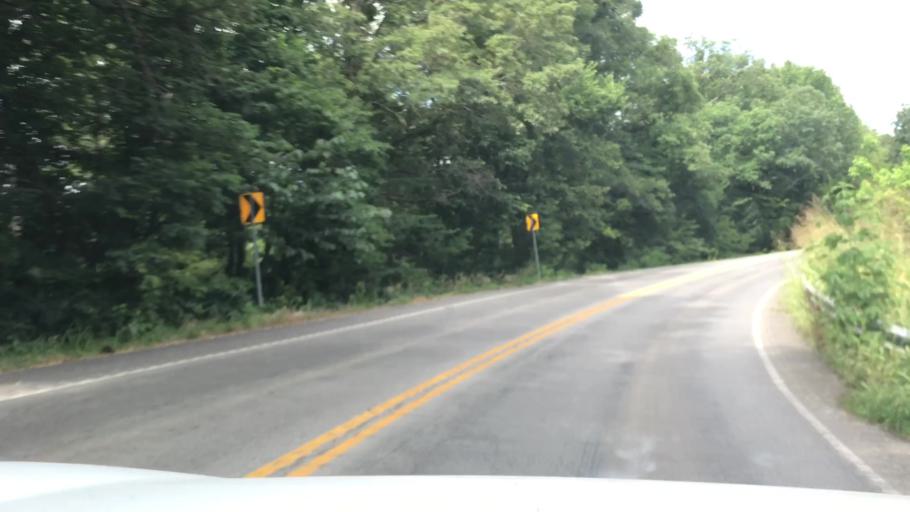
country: US
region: Missouri
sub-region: Saint Charles County
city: Weldon Spring
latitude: 38.6631
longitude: -90.7431
